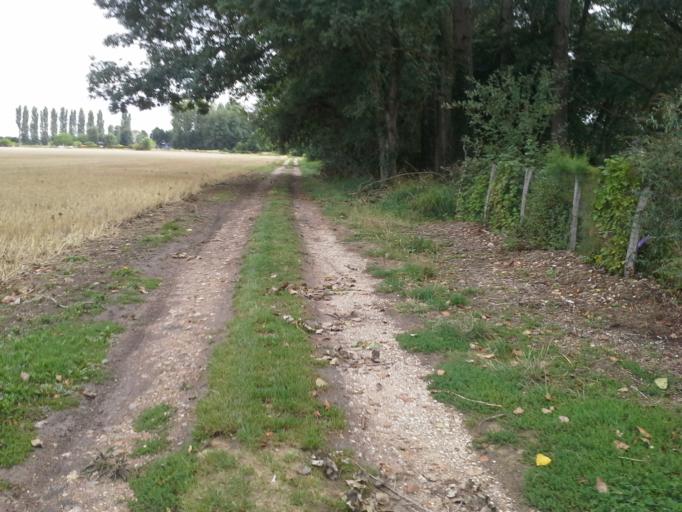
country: FR
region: Centre
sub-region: Departement du Loir-et-Cher
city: Villiers-sur-Loir
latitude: 47.8066
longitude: 0.9786
